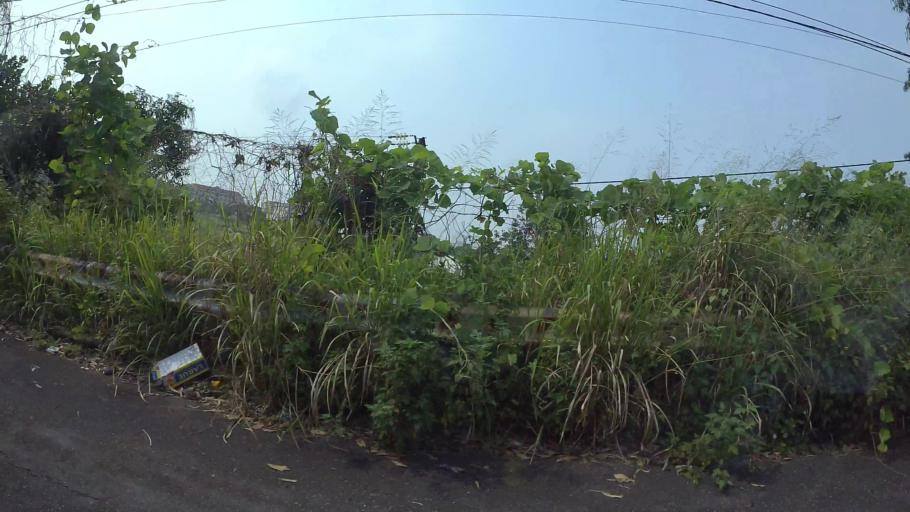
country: VN
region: Da Nang
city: Son Tra
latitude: 16.1091
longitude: 108.2606
